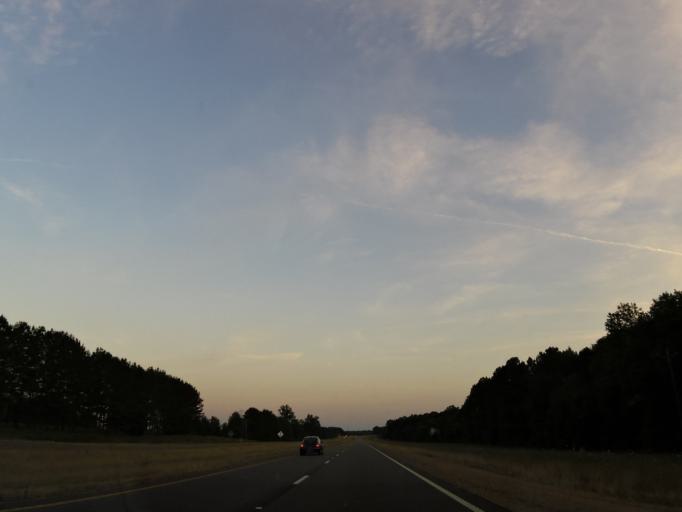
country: US
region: Mississippi
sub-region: Kemper County
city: De Kalb
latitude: 32.8232
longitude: -88.4602
